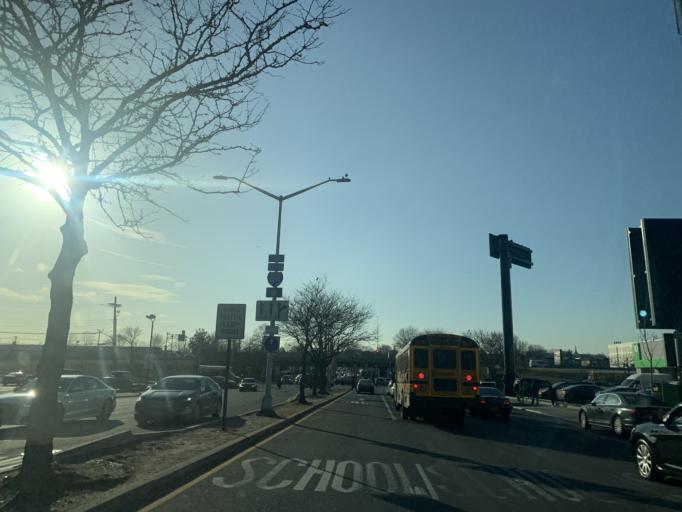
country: US
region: New York
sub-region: Bronx
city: Eastchester
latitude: 40.8691
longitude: -73.8309
